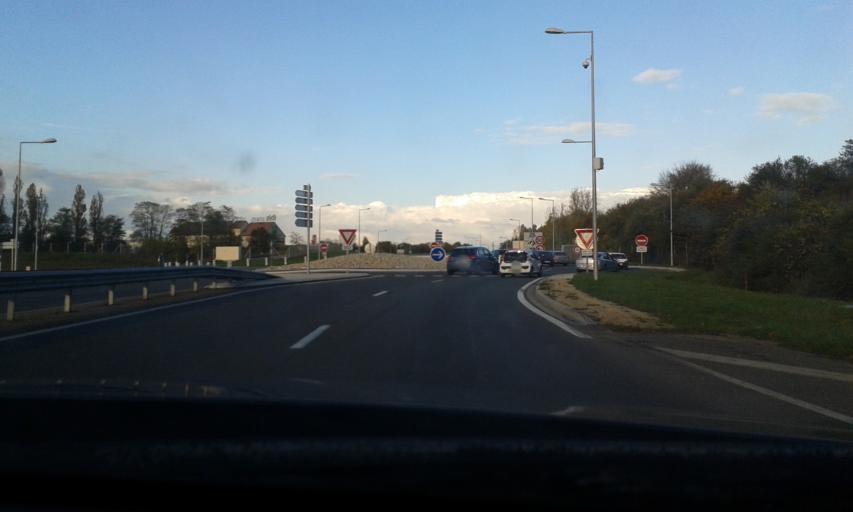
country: FR
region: Centre
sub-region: Departement d'Eure-et-Loir
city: Le Coudray
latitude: 48.4245
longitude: 1.5129
